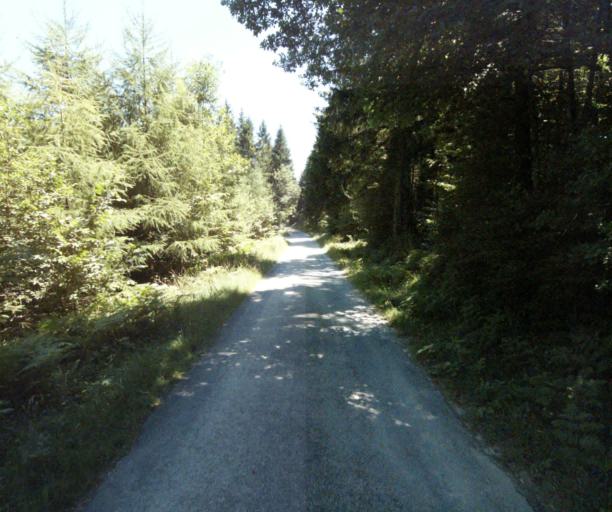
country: FR
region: Languedoc-Roussillon
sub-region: Departement de l'Aude
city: Cuxac-Cabardes
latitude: 43.4027
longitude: 2.2098
